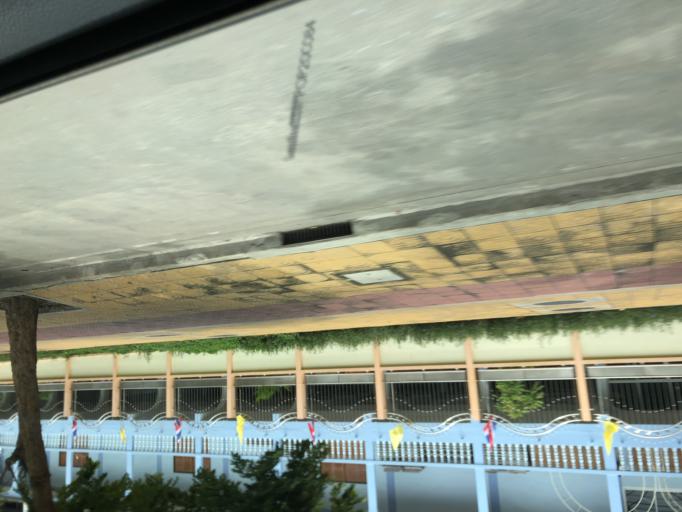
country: TH
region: Bangkok
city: Don Mueang
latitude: 13.9247
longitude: 100.5953
